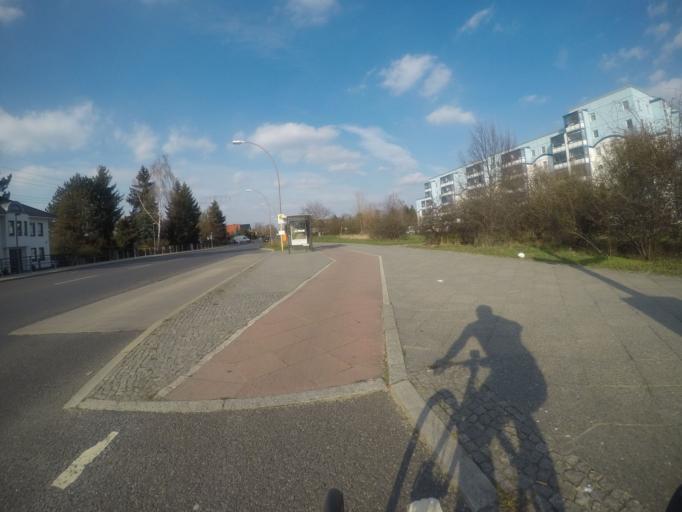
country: DE
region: Berlin
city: Altglienicke
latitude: 52.4068
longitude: 13.5252
